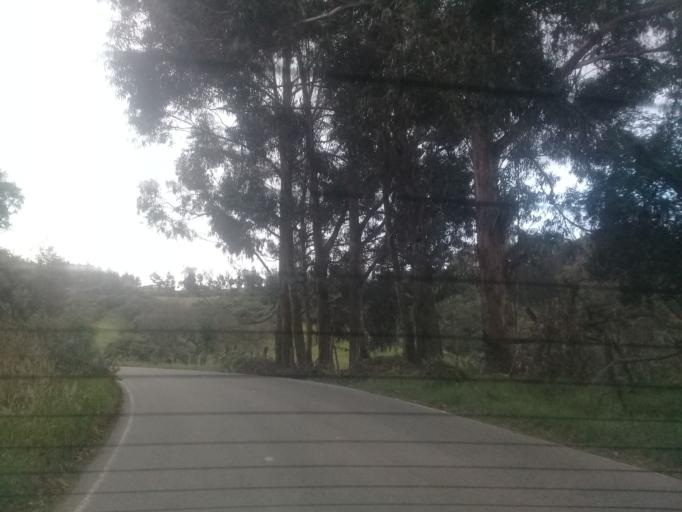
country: CO
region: Cundinamarca
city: Tabio
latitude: 4.9430
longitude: -74.1073
